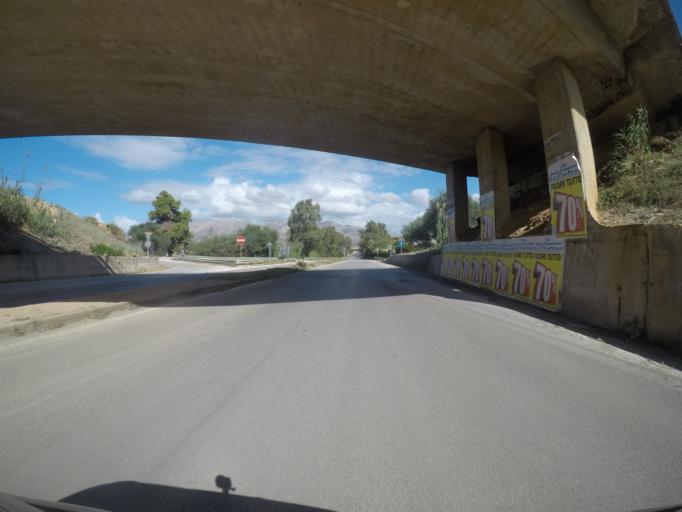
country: IT
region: Sicily
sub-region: Palermo
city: Trappeto
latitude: 38.0695
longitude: 13.0527
